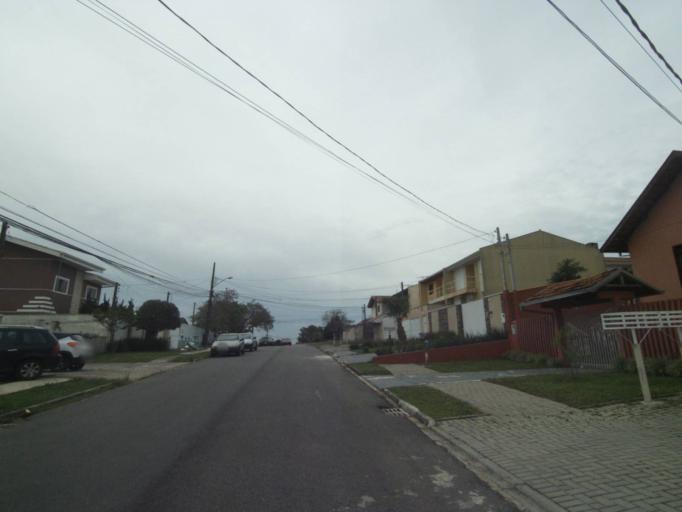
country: BR
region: Parana
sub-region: Pinhais
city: Pinhais
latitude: -25.4199
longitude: -49.2067
